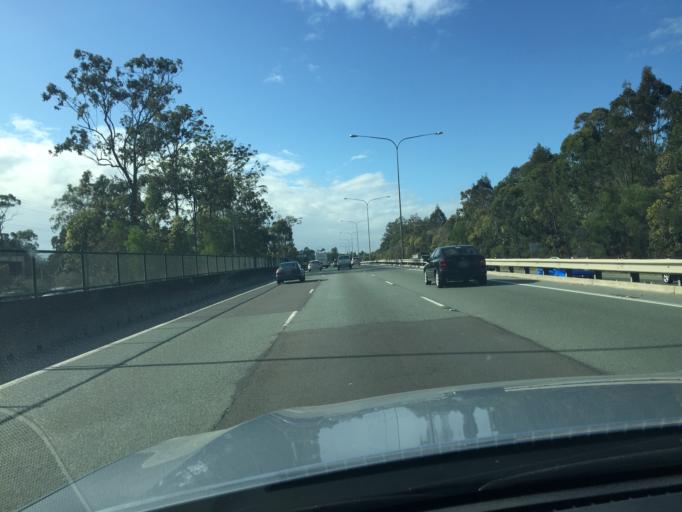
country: AU
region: Queensland
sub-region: Logan
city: Slacks Creek
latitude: -27.6710
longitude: 153.1796
